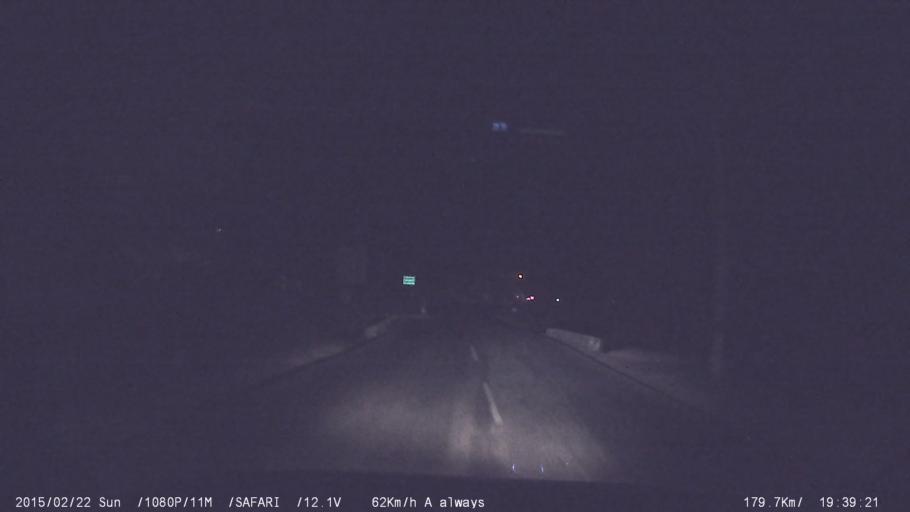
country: IN
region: Tamil Nadu
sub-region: Theni
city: Devadanappatti
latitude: 10.1457
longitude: 77.6372
